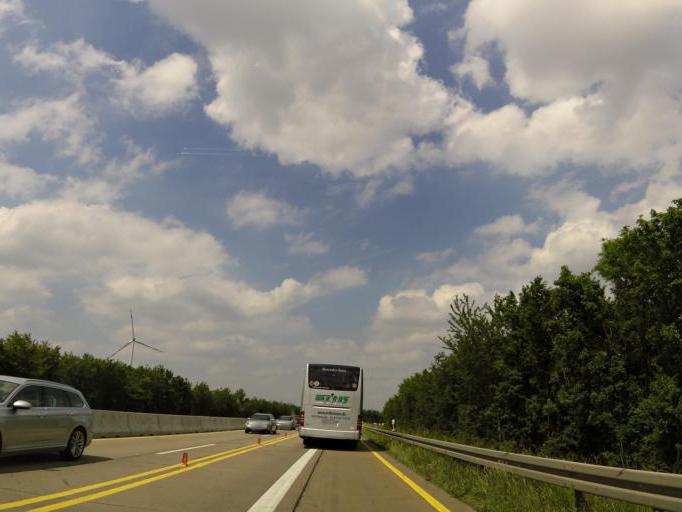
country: DE
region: Bavaria
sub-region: Regierungsbezirk Mittelfranken
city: Simmershofen
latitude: 49.5467
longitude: 10.1646
